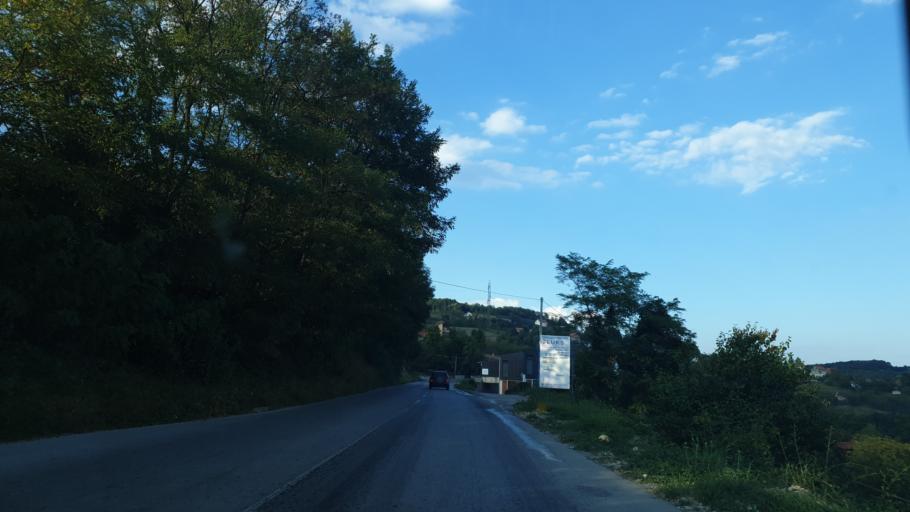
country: RS
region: Central Serbia
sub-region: Zlatiborski Okrug
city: Uzice
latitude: 43.8582
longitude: 19.8774
